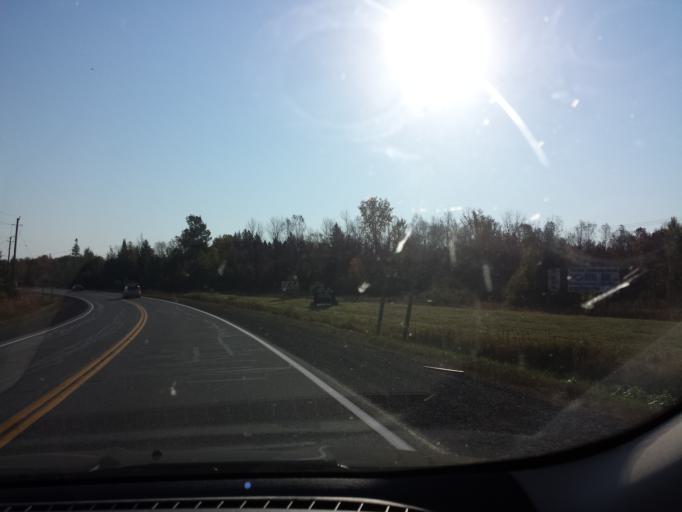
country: CA
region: Ontario
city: Prescott
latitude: 45.0281
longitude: -75.6203
